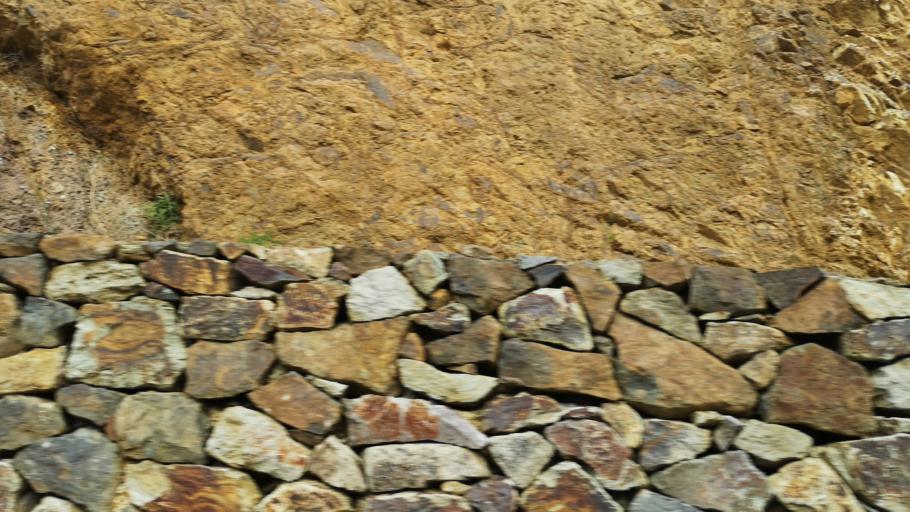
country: ES
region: Canary Islands
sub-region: Provincia de Santa Cruz de Tenerife
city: Vallehermosa
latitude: 28.1724
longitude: -17.2750
